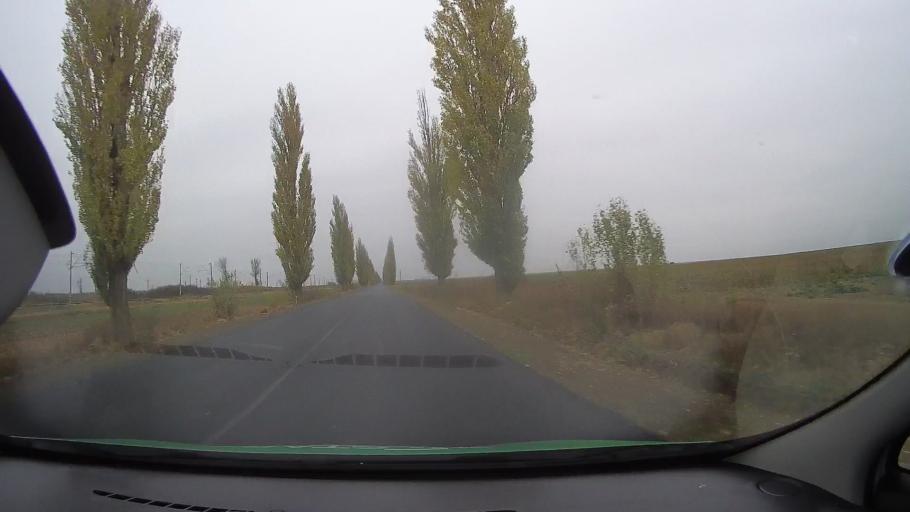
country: RO
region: Ialomita
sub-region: Comuna Valea Ciorii
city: Valea Ciorii
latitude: 44.7102
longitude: 27.5925
